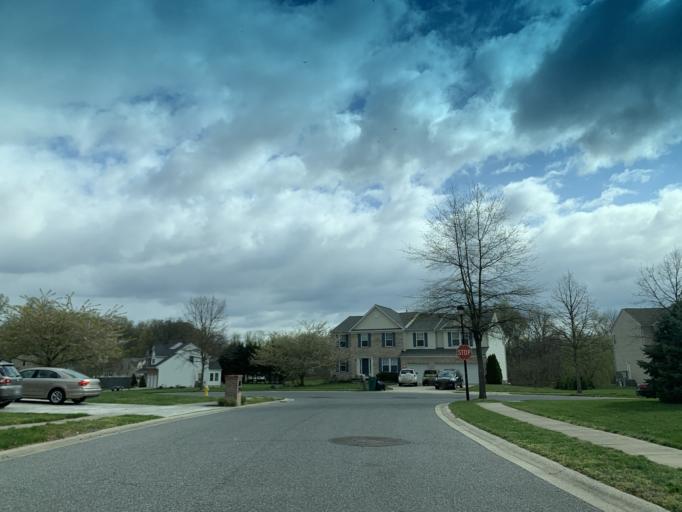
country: US
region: Maryland
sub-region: Harford County
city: South Bel Air
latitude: 39.5561
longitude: -76.3048
